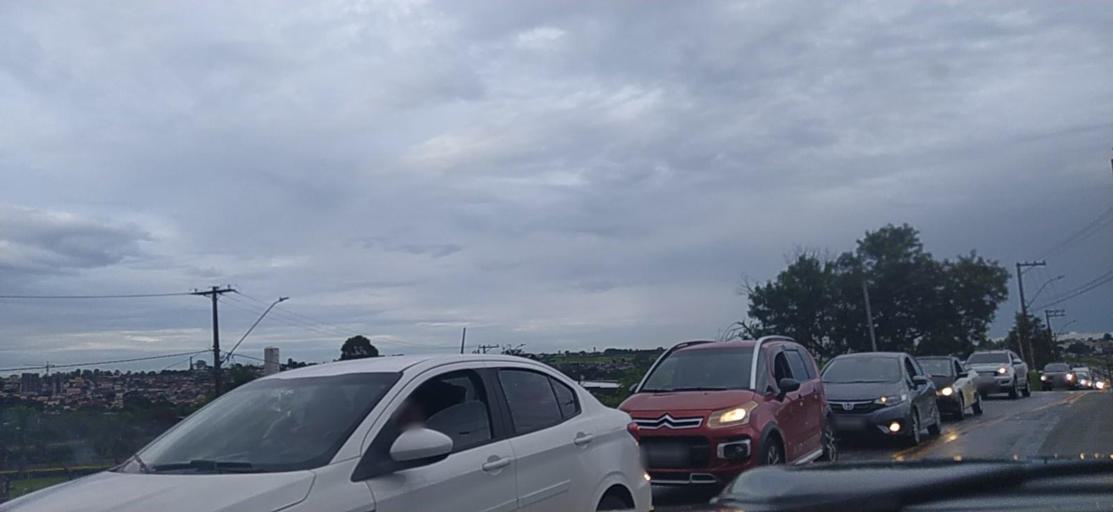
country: BR
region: Sao Paulo
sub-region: Hortolandia
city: Hortolandia
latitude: -22.8924
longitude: -47.1767
